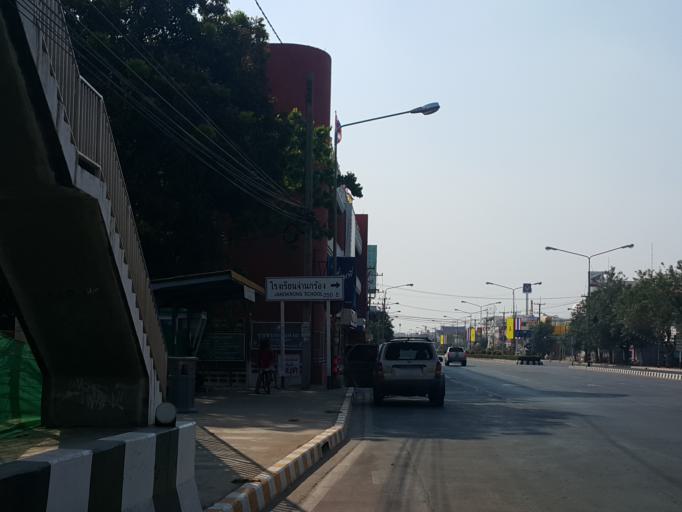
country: TH
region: Phitsanulok
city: Phitsanulok
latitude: 16.8238
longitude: 100.2588
